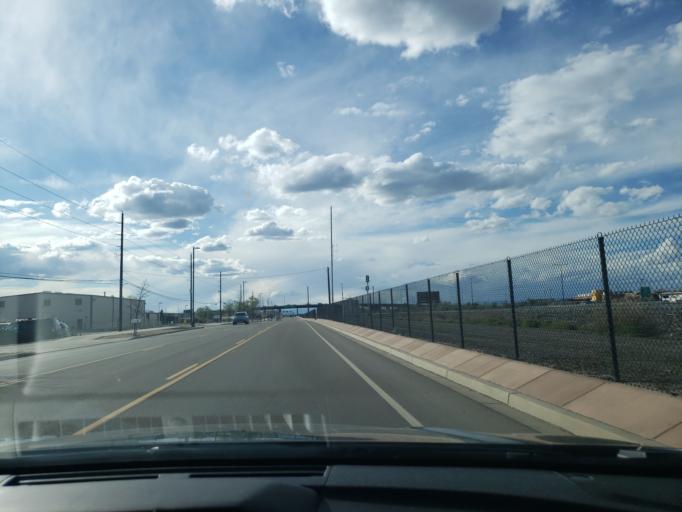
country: US
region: Colorado
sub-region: Mesa County
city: Redlands
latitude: 39.0887
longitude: -108.6044
